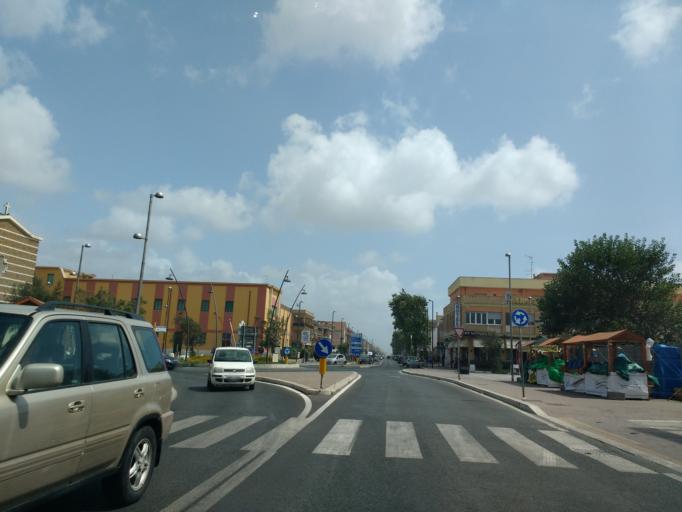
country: IT
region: Latium
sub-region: Citta metropolitana di Roma Capitale
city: Torvaianica
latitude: 41.6210
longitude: 12.4624
